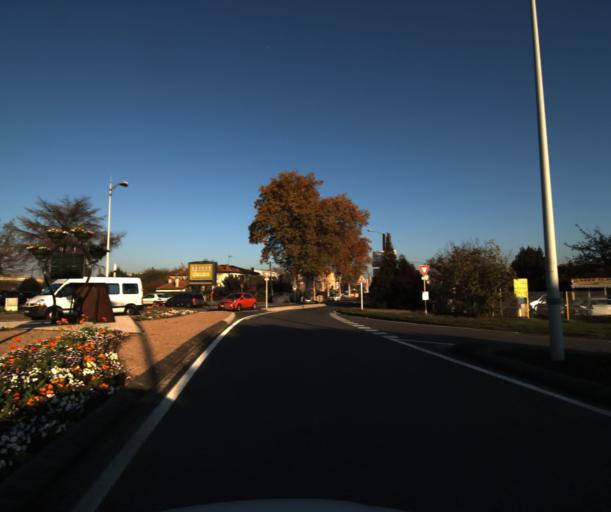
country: FR
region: Midi-Pyrenees
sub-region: Departement de la Haute-Garonne
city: Colomiers
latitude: 43.6093
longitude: 1.3527
